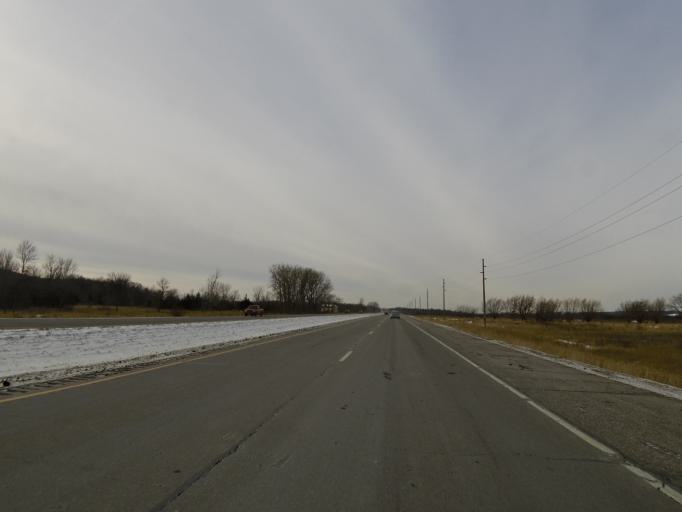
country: US
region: Minnesota
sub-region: Scott County
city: Jordan
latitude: 44.6507
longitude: -93.6926
